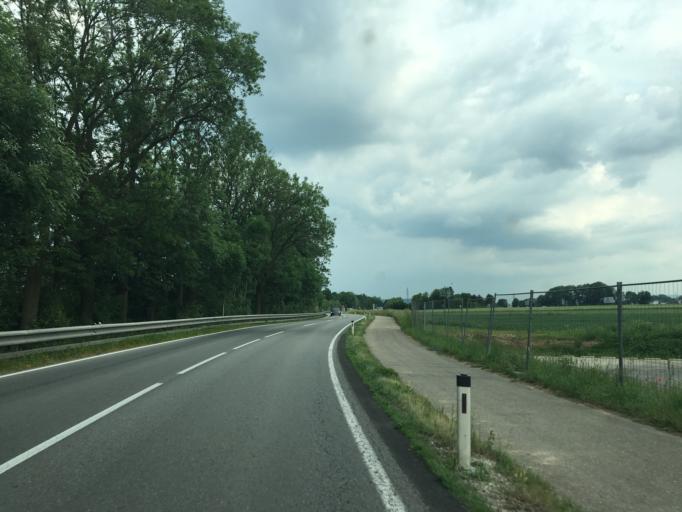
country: AT
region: Upper Austria
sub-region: Politischer Bezirk Braunau am Inn
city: Braunau am Inn
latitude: 48.1445
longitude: 13.1324
